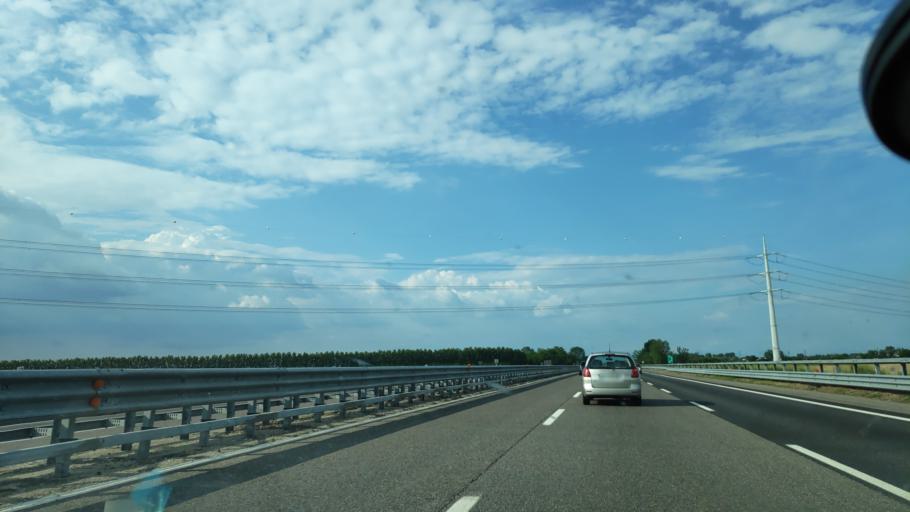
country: IT
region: Lombardy
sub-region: Citta metropolitana di Milano
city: Vernate
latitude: 45.3017
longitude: 9.0702
